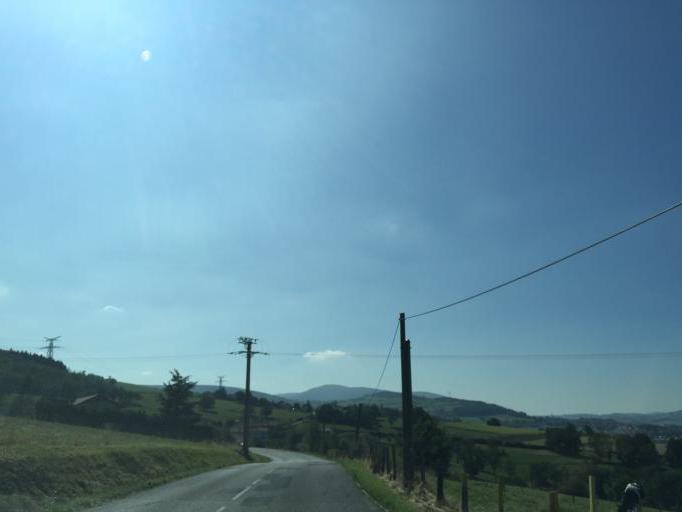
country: FR
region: Rhone-Alpes
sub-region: Departement de la Loire
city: Saint-Paul-en-Jarez
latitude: 45.4760
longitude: 4.5669
